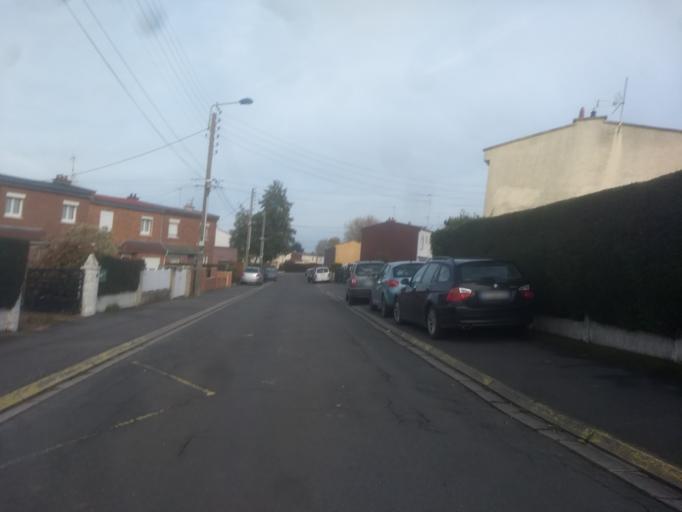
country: FR
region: Nord-Pas-de-Calais
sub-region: Departement du Pas-de-Calais
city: Beaurains
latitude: 50.2680
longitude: 2.7889
